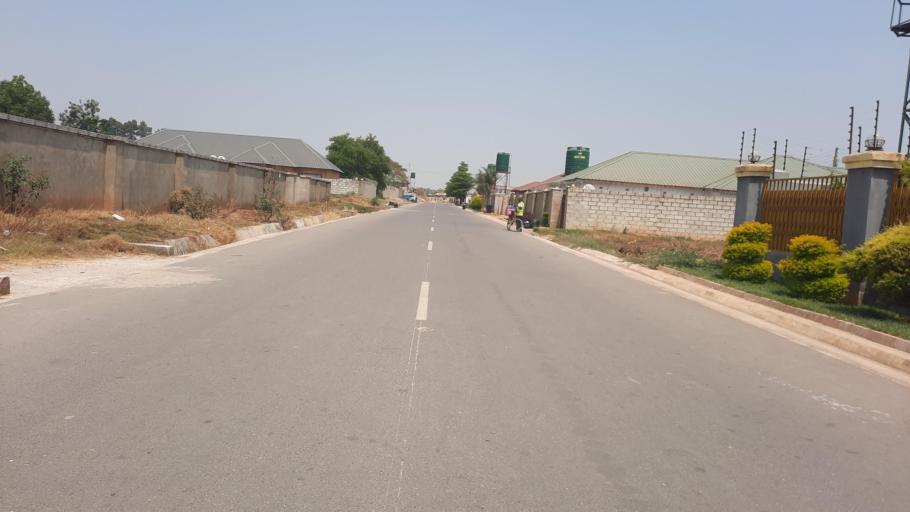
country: ZM
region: Lusaka
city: Lusaka
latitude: -15.3949
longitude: 28.3889
